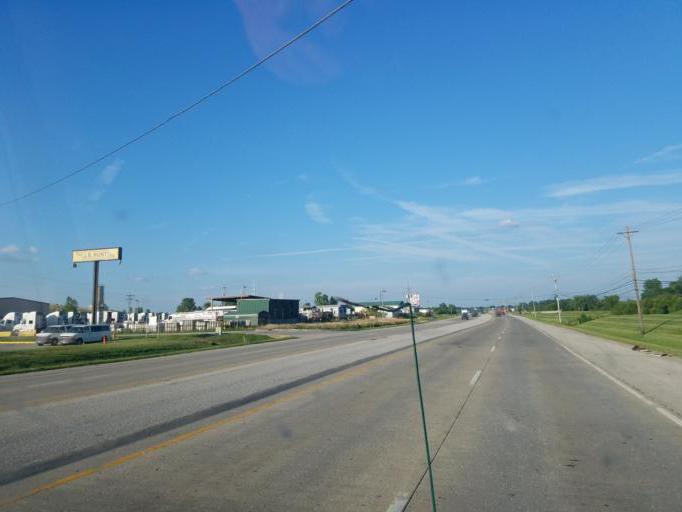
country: US
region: Kentucky
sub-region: Jefferson County
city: Heritage Creek
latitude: 38.1312
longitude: -85.7314
